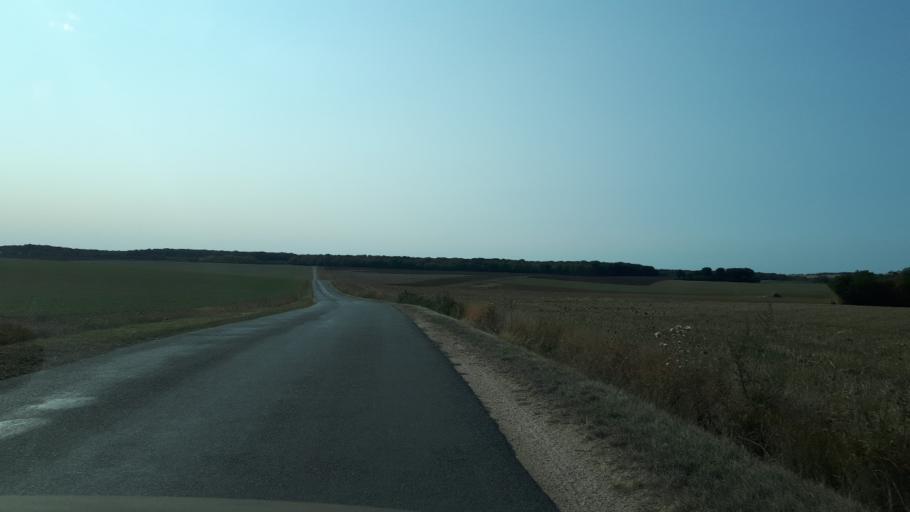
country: FR
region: Centre
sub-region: Departement du Cher
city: Rians
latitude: 47.1849
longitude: 2.6685
